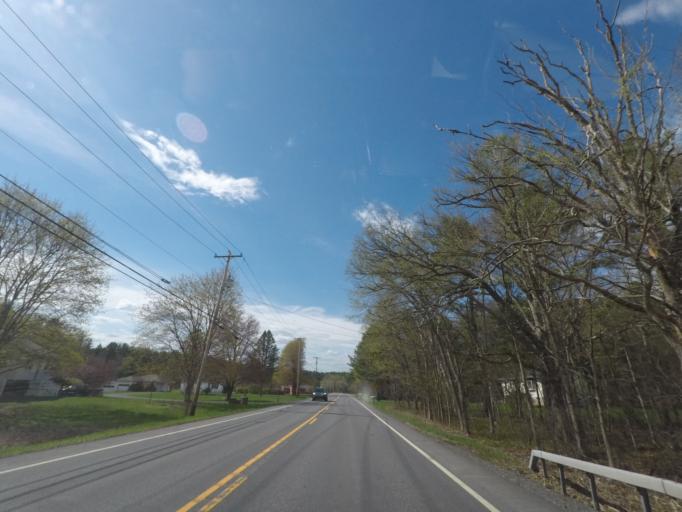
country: US
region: New York
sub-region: Greene County
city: Cairo
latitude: 42.3136
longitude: -74.0096
